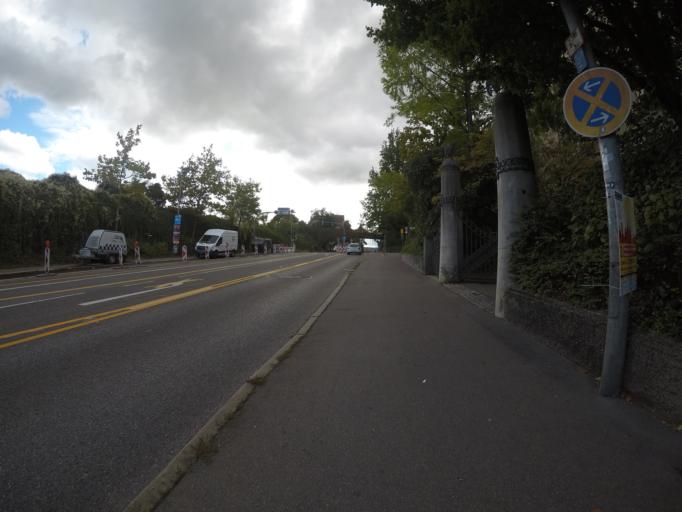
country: DE
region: Baden-Wuerttemberg
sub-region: Tuebingen Region
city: Reutlingen
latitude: 48.4885
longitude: 9.2069
